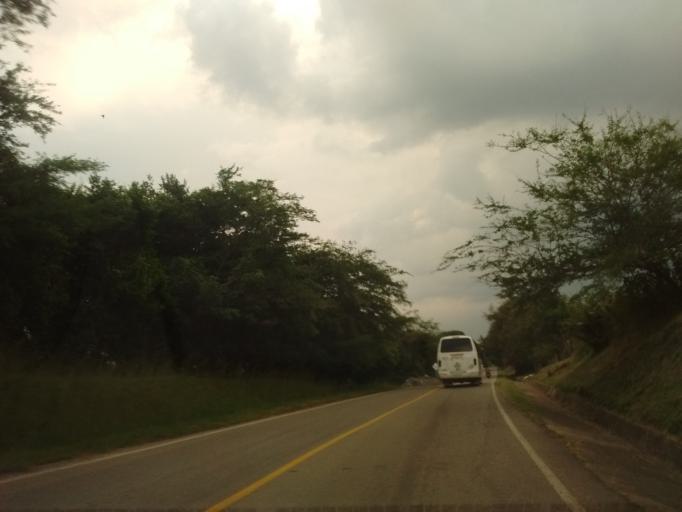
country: CO
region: Cauca
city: Caloto
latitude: 3.0604
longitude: -76.3705
